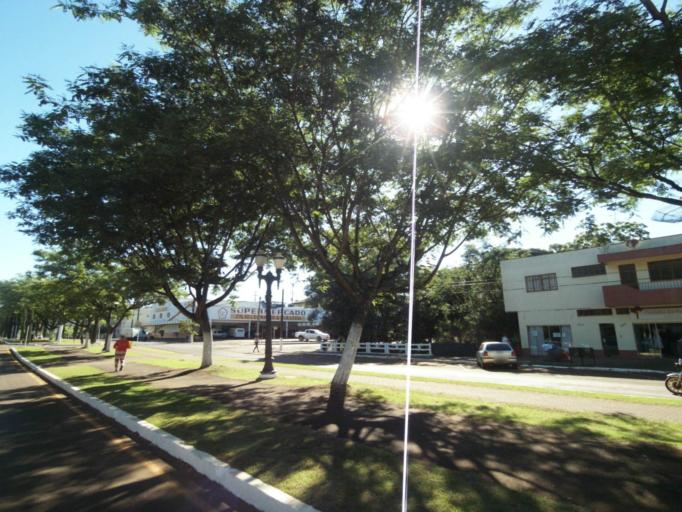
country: BR
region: Parana
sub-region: Pato Branco
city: Pato Branco
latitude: -26.2652
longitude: -52.7810
